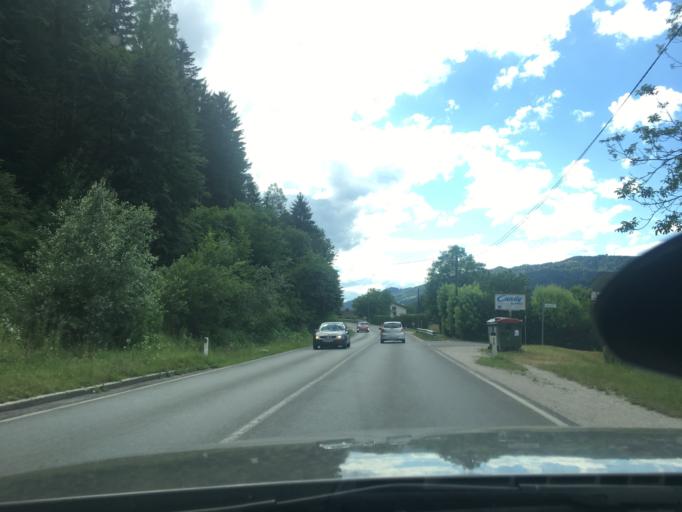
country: SI
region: Ruse
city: Bistrica ob Dravi
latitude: 46.5534
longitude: 15.5466
